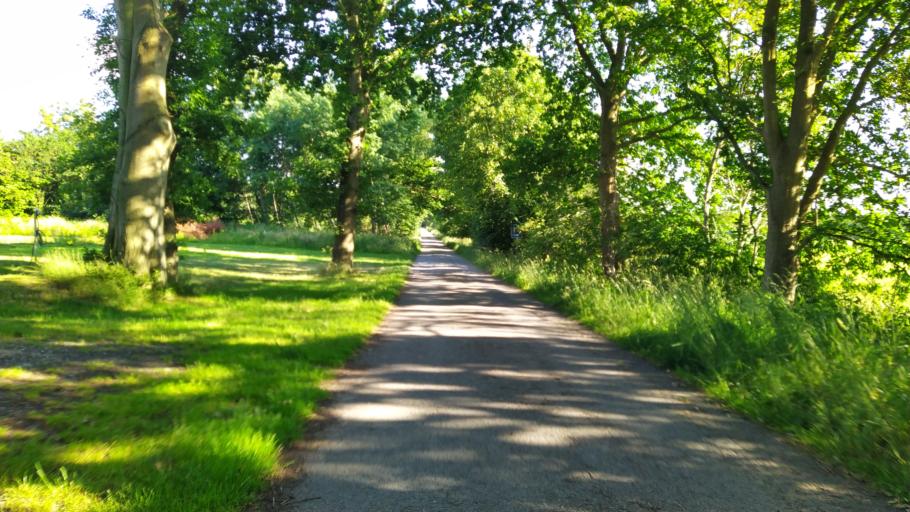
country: DE
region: Lower Saxony
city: Lintig
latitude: 53.5927
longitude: 8.9280
